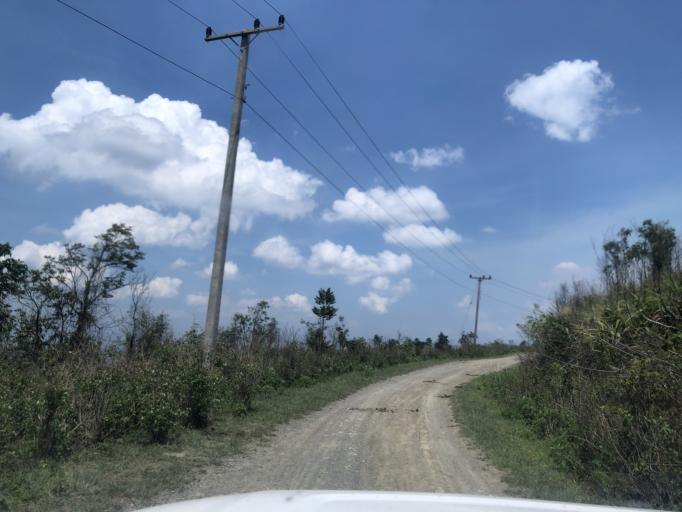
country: LA
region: Phongsali
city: Phongsali
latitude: 21.4213
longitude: 102.1826
